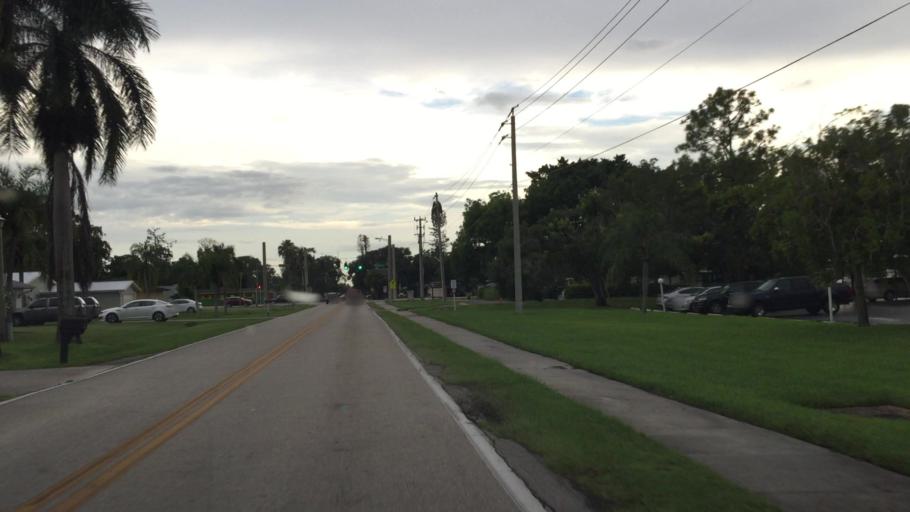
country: US
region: Florida
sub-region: Lee County
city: Pine Manor
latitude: 26.5659
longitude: -81.8682
